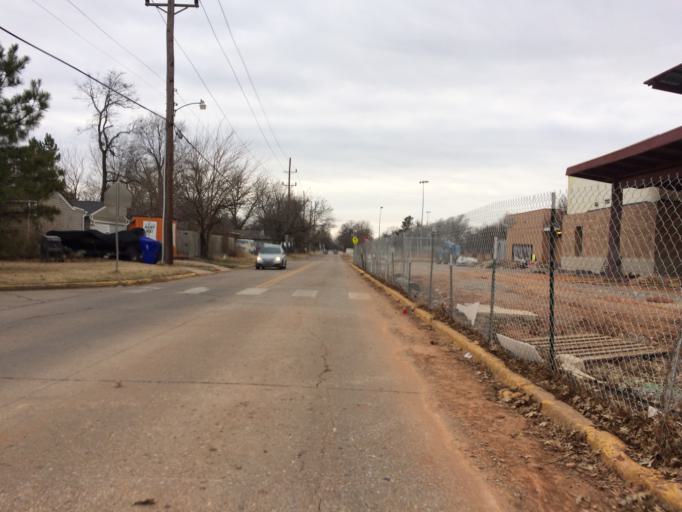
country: US
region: Oklahoma
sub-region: Cleveland County
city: Norman
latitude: 35.2136
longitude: -97.4634
